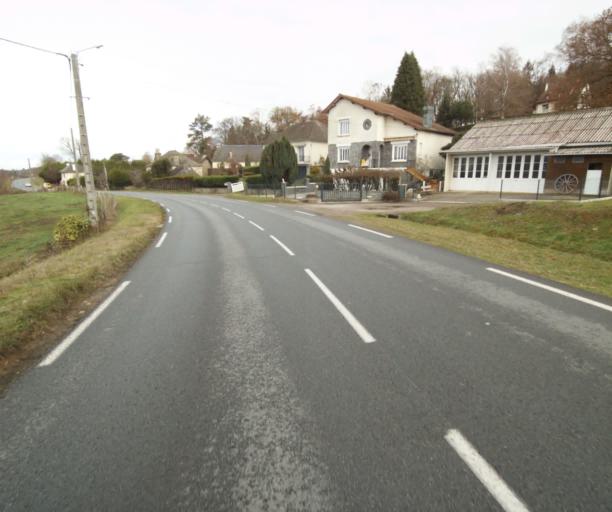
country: FR
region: Limousin
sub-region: Departement de la Correze
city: Saint-Mexant
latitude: 45.2669
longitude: 1.6374
